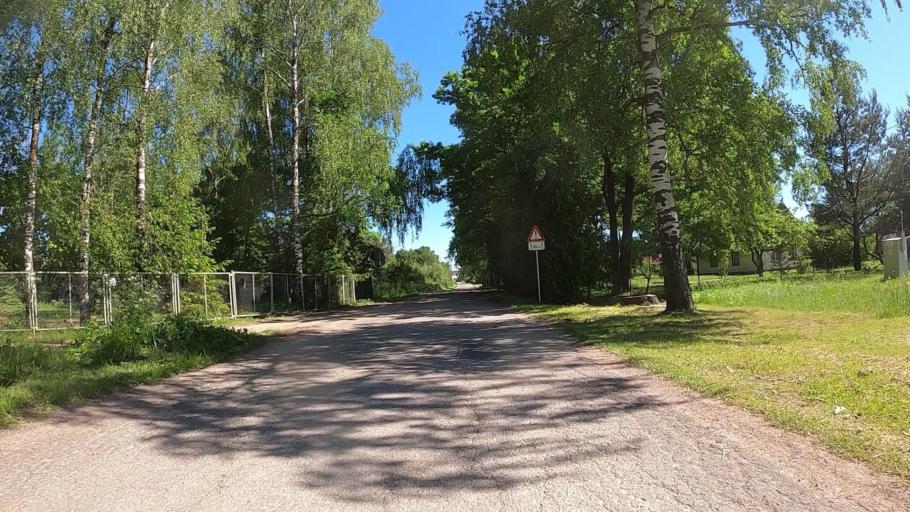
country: LV
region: Salaspils
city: Salaspils
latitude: 56.8785
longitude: 24.3268
